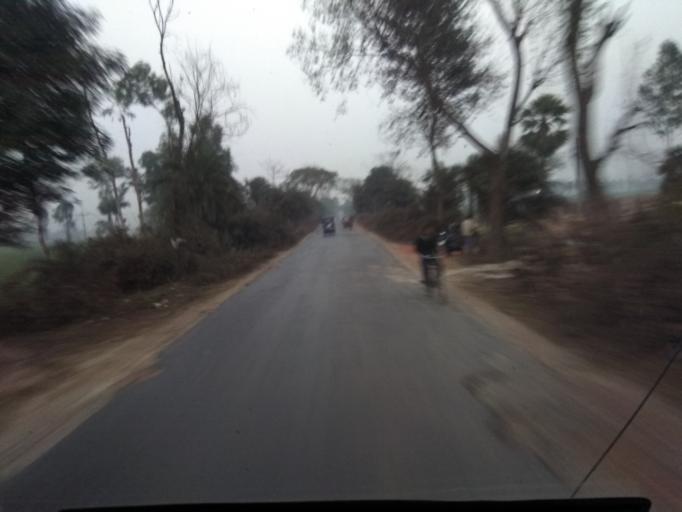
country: BD
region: Rajshahi
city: Bogra
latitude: 24.7431
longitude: 89.3354
